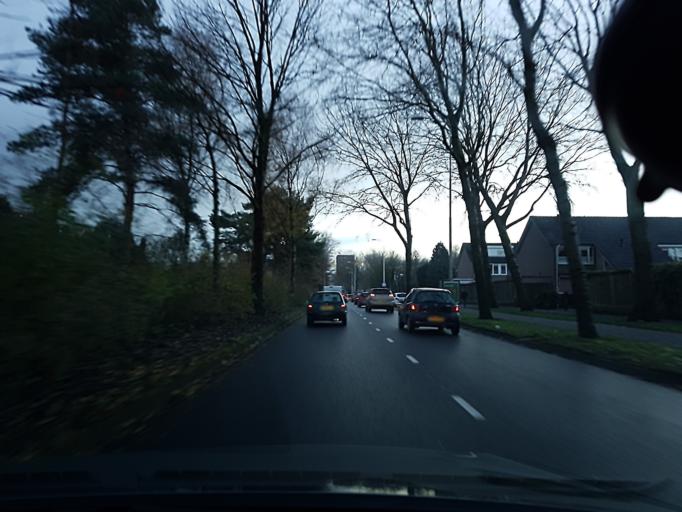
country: NL
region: North Brabant
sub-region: Gemeente Waalre
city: Waalre
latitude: 51.4178
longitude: 5.4374
